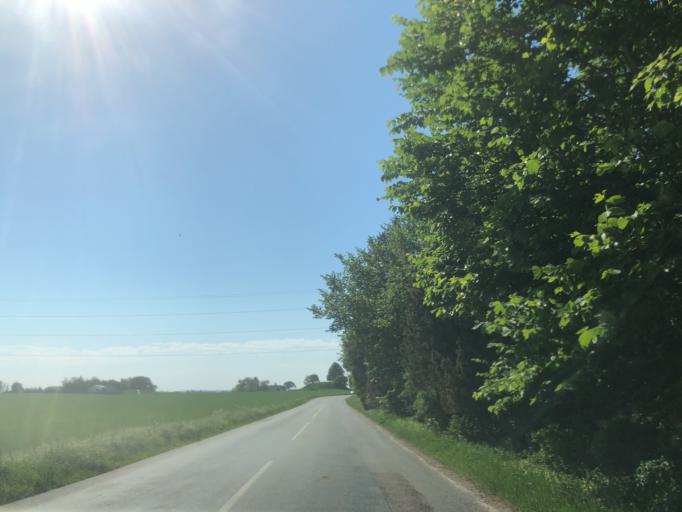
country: DK
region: Zealand
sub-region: Roskilde Kommune
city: Viby
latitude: 55.5717
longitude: 12.0573
